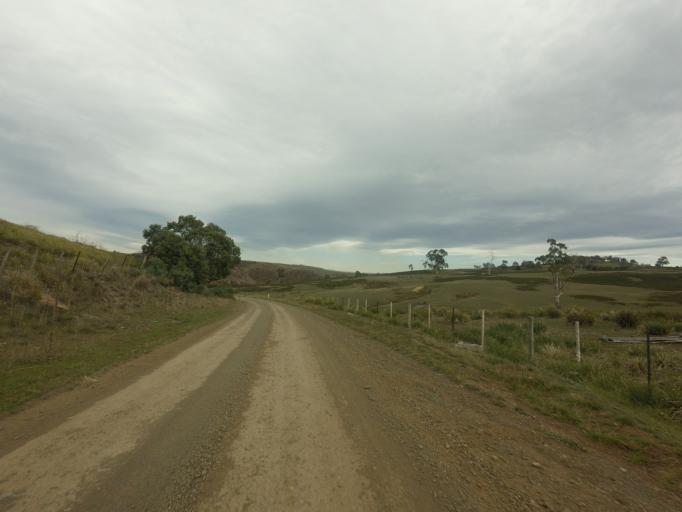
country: AU
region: Tasmania
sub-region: Derwent Valley
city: New Norfolk
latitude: -42.4033
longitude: 146.9483
